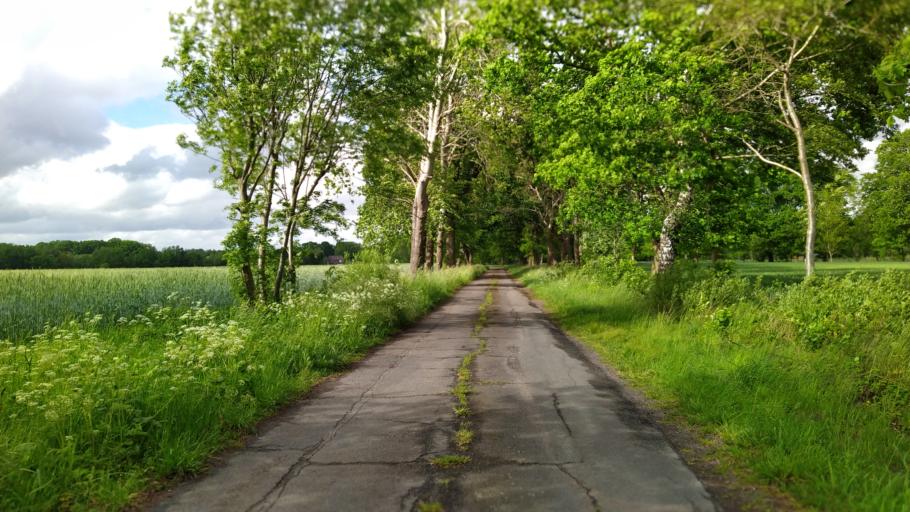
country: DE
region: Lower Saxony
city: Farven
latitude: 53.4267
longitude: 9.3532
